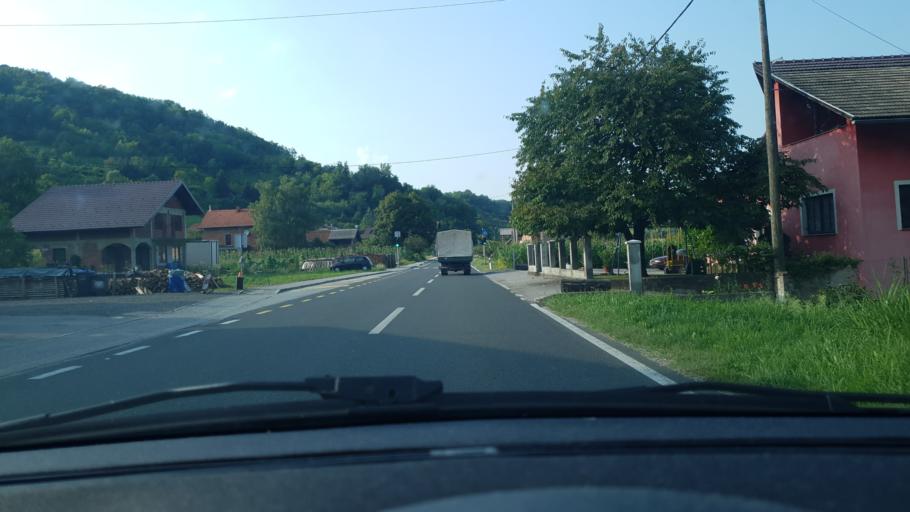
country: HR
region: Krapinsko-Zagorska
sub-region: Grad Krapina
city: Krapina
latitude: 46.1097
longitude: 15.9062
